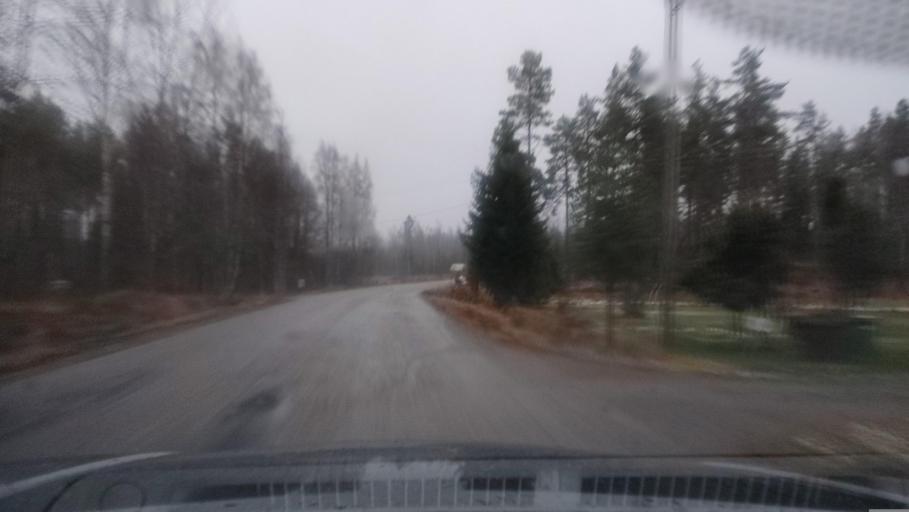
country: FI
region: Southern Ostrobothnia
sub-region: Suupohja
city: Karijoki
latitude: 62.1410
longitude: 21.5723
